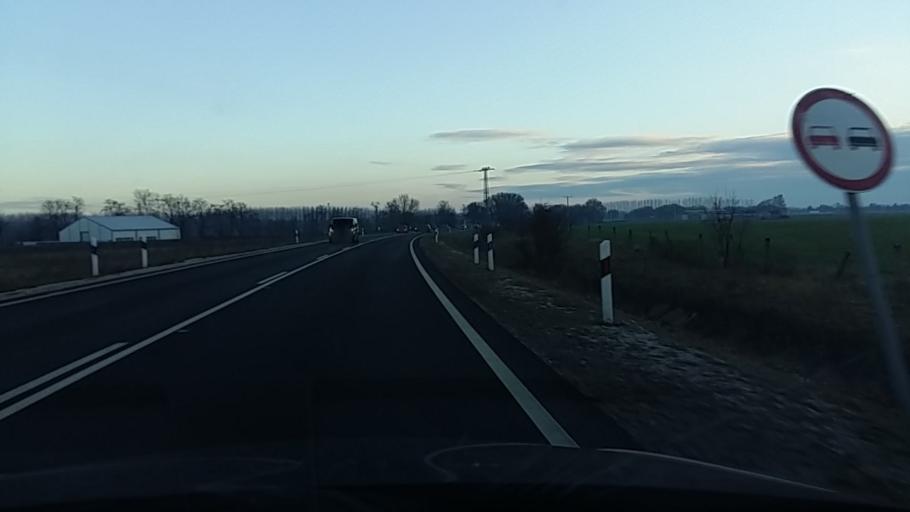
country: HU
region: Hajdu-Bihar
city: Hajduhadhaz
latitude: 47.6609
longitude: 21.6592
